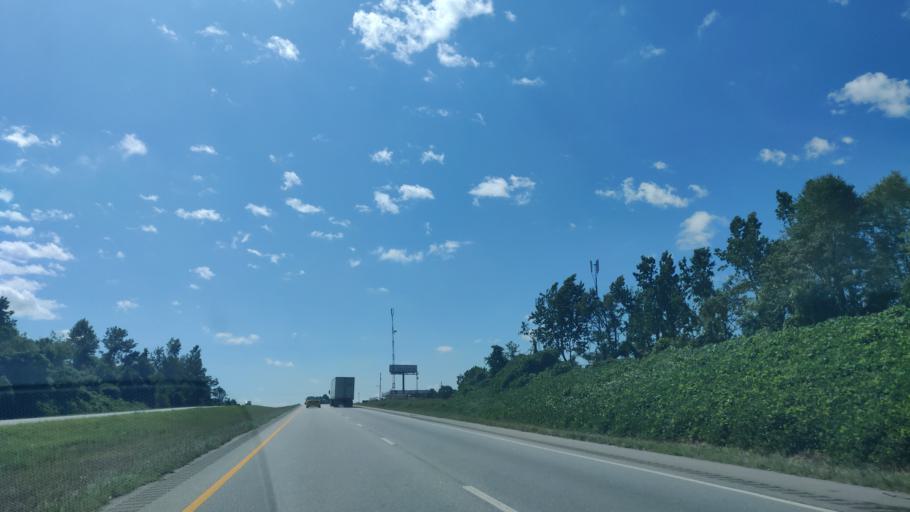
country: US
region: Alabama
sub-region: Lee County
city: Smiths Station
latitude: 32.5501
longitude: -85.1058
